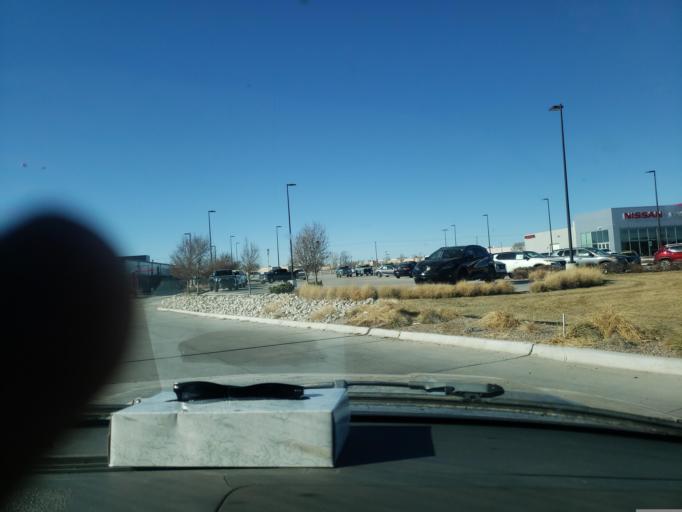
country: US
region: Kansas
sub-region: Finney County
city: Garden City
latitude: 37.9750
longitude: -100.8365
